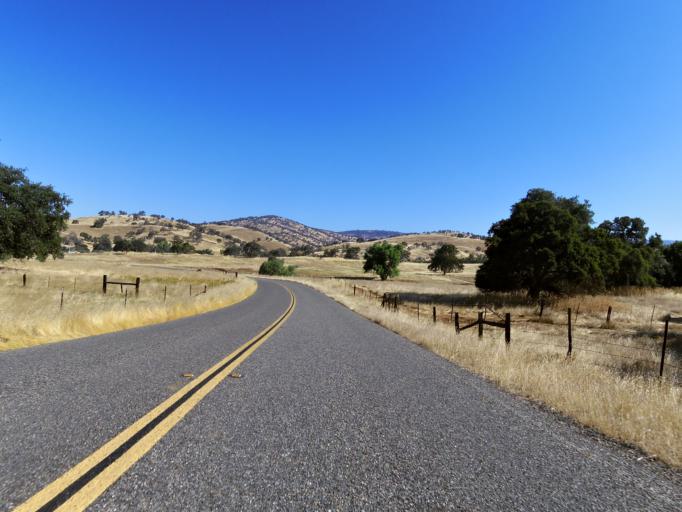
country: US
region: California
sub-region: Mariposa County
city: Mariposa
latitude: 37.4896
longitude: -120.1386
